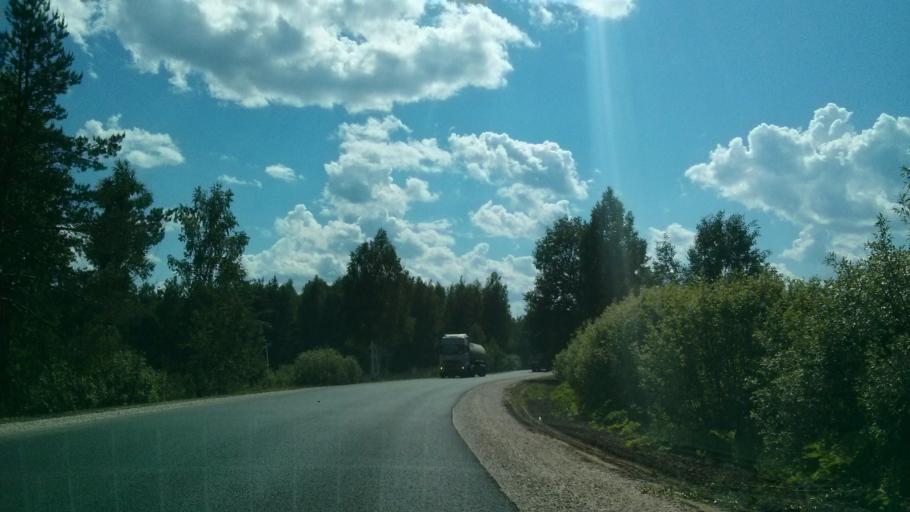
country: RU
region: Vladimir
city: Murom
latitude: 55.4990
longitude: 41.9066
